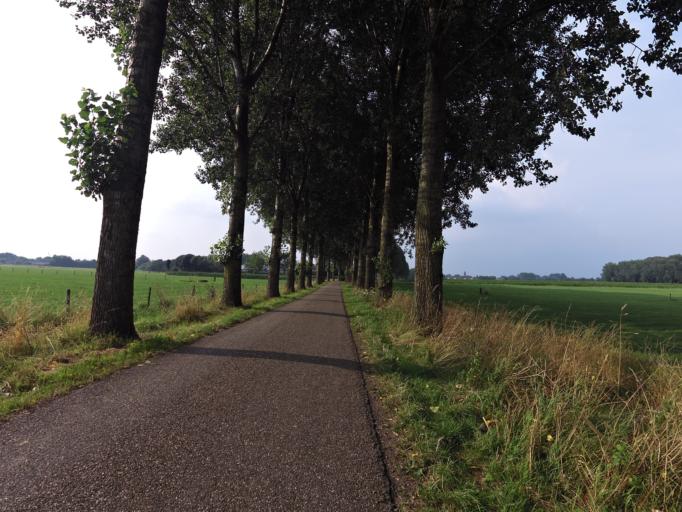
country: NL
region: Gelderland
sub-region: Gemeente Rheden
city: De Steeg
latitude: 51.9841
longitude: 6.0684
